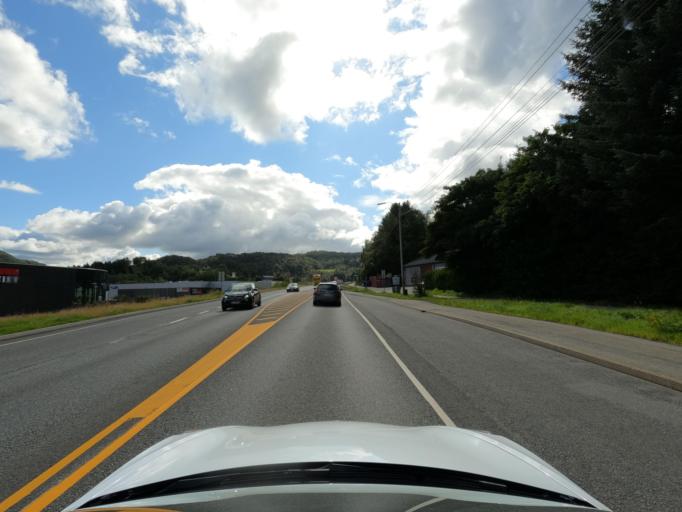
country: NO
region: Hordaland
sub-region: Bergen
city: Hylkje
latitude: 60.4869
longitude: 5.3764
